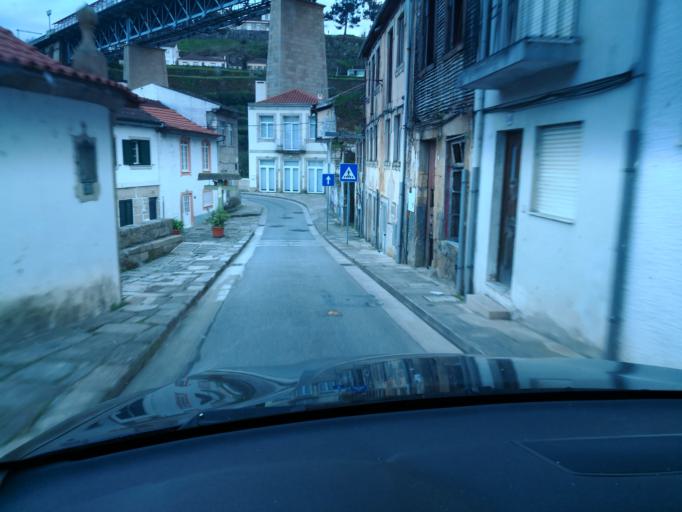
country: PT
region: Vila Real
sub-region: Vila Real
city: Vila Real
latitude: 41.2975
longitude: -7.7404
